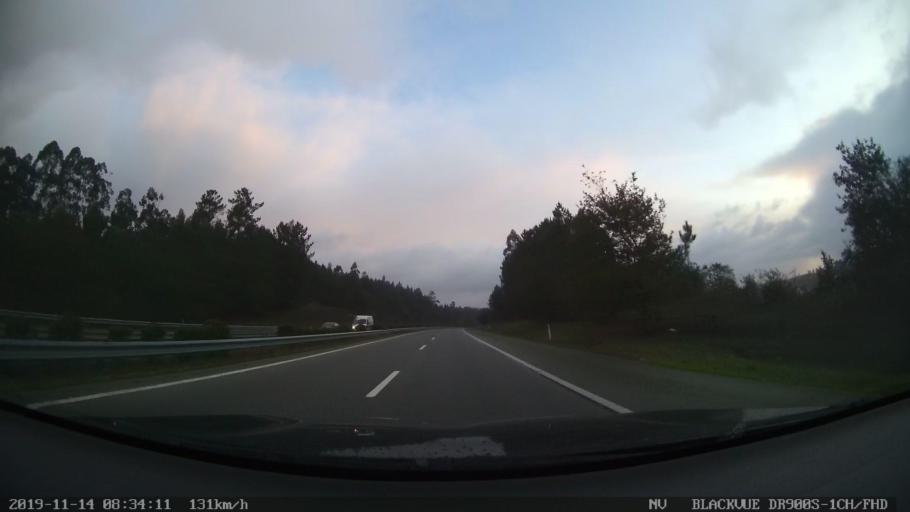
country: PT
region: Braga
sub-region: Barcelos
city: Galegos
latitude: 41.6385
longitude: -8.5592
